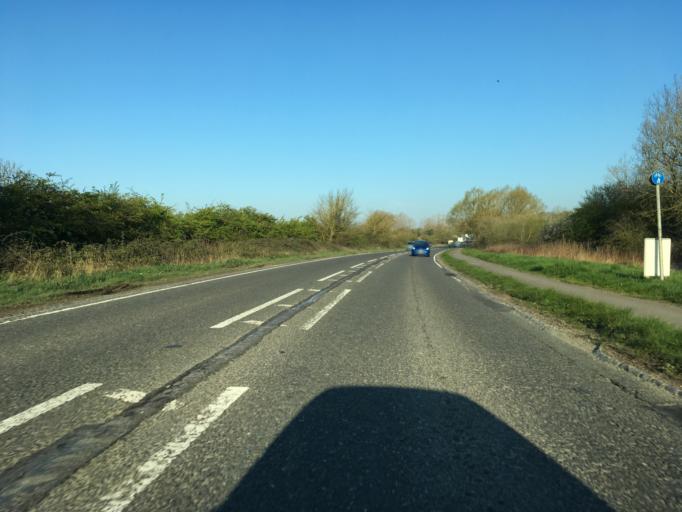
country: GB
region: England
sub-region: Oxfordshire
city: Eynsham
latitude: 51.7887
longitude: -1.3997
